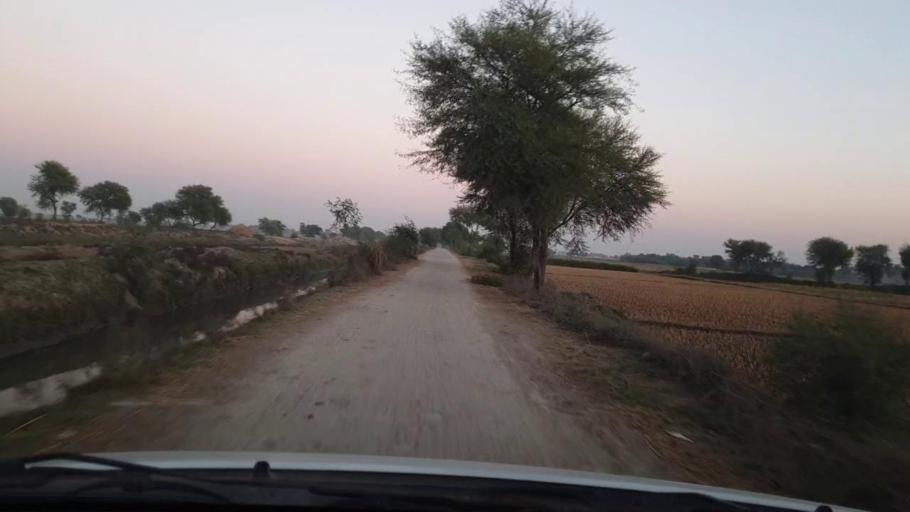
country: PK
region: Sindh
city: Khairpur Nathan Shah
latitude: 27.1512
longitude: 67.6913
